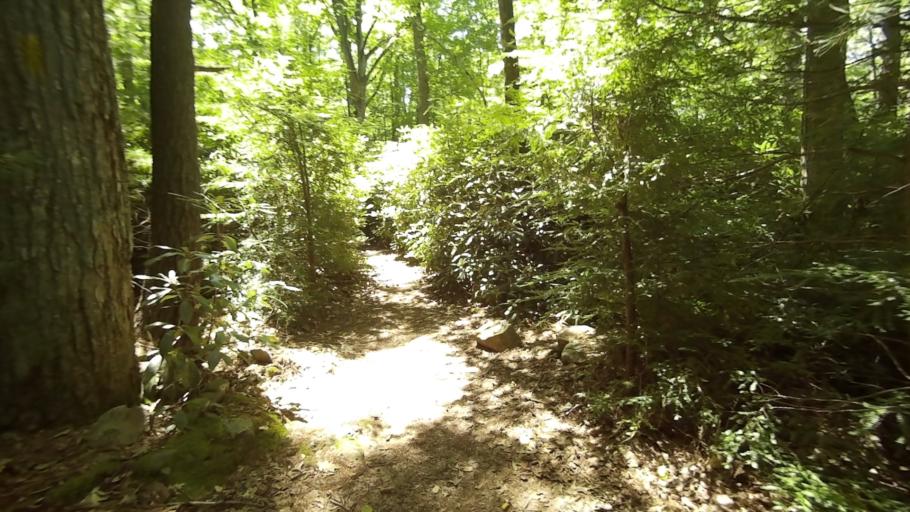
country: US
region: Pennsylvania
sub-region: Centre County
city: Boalsburg
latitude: 40.7303
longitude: -77.7557
